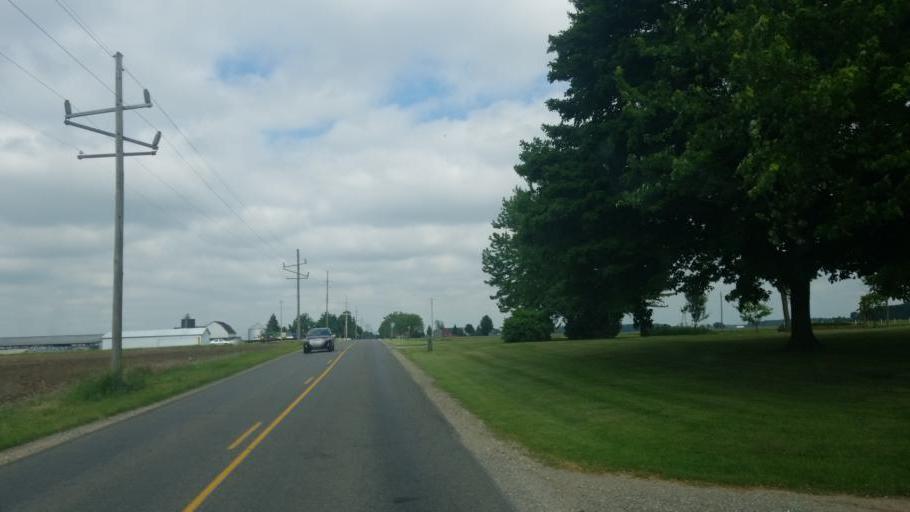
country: US
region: Indiana
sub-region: Elkhart County
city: Wakarusa
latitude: 41.4935
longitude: -86.0229
